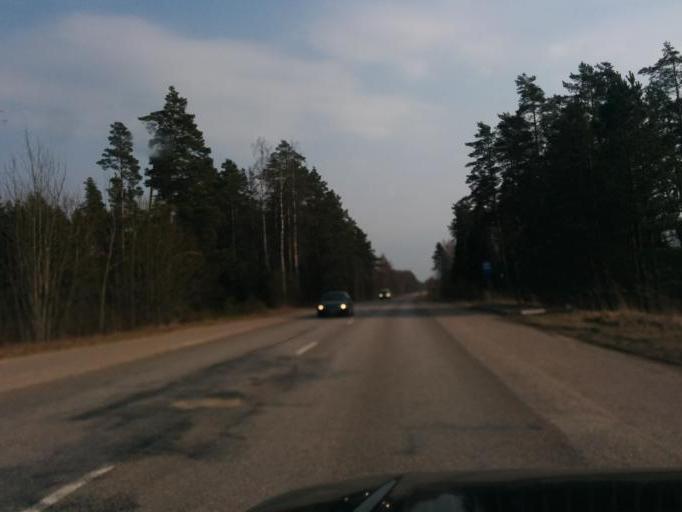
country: LV
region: Kekava
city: Balozi
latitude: 56.7829
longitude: 24.0933
